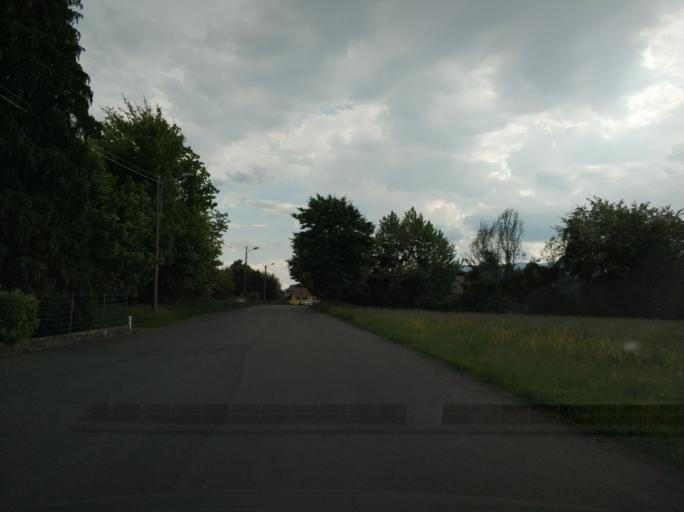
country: IT
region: Piedmont
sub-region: Provincia di Torino
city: Mathi
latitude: 45.2632
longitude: 7.5464
